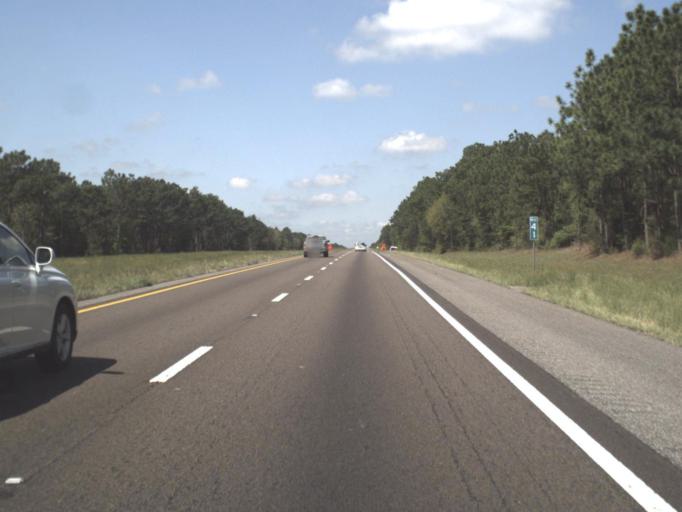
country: US
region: Florida
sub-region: Santa Rosa County
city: East Milton
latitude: 30.6794
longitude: -86.8143
